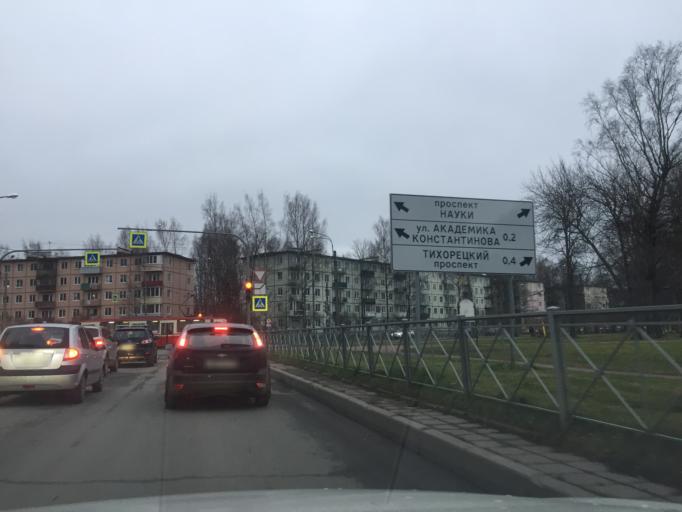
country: RU
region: Leningrad
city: Akademicheskoe
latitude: 60.0182
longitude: 30.3741
